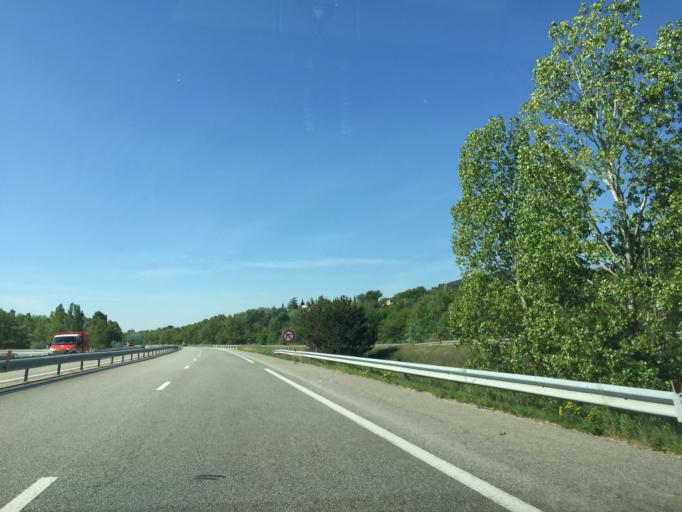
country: FR
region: Provence-Alpes-Cote d'Azur
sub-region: Departement des Alpes-de-Haute-Provence
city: Oraison
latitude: 43.9209
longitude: 5.8925
